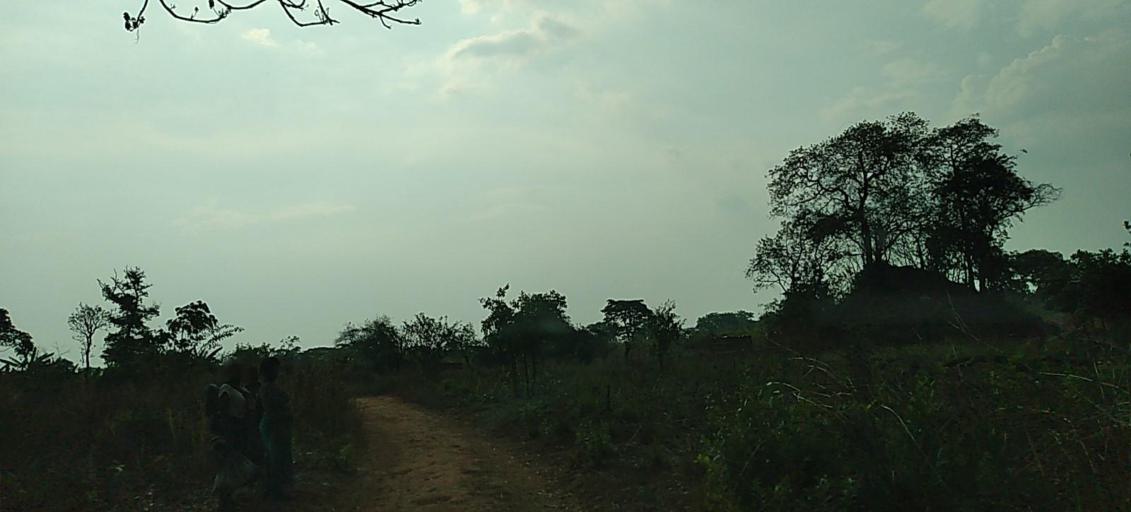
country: ZM
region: North-Western
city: Solwezi
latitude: -12.0549
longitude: 26.1533
